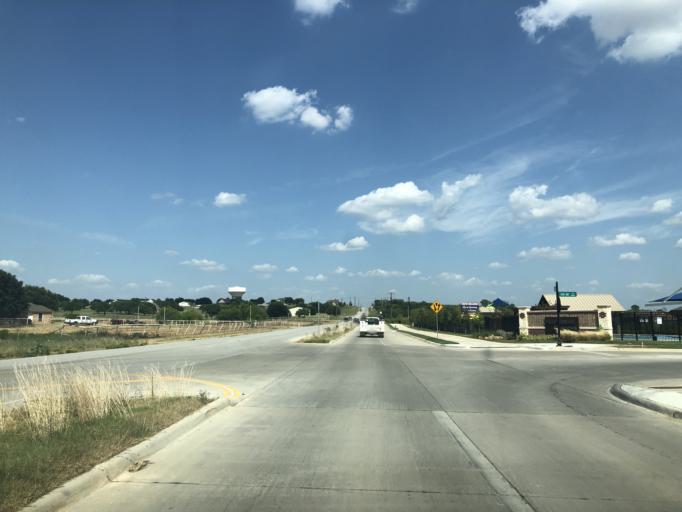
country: US
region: Texas
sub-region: Tarrant County
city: Haslet
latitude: 32.9242
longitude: -97.3417
